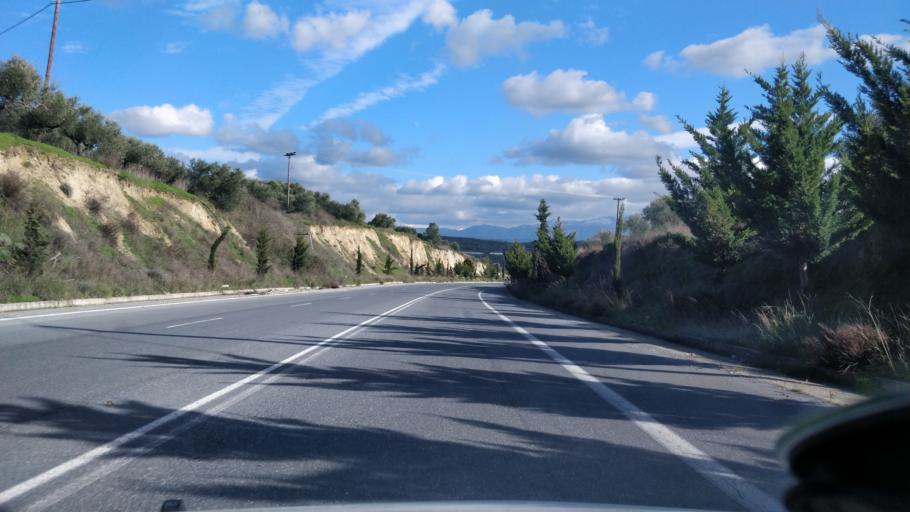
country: GR
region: Crete
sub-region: Nomos Irakleiou
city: Ano Arhanes
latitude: 35.2245
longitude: 25.1887
